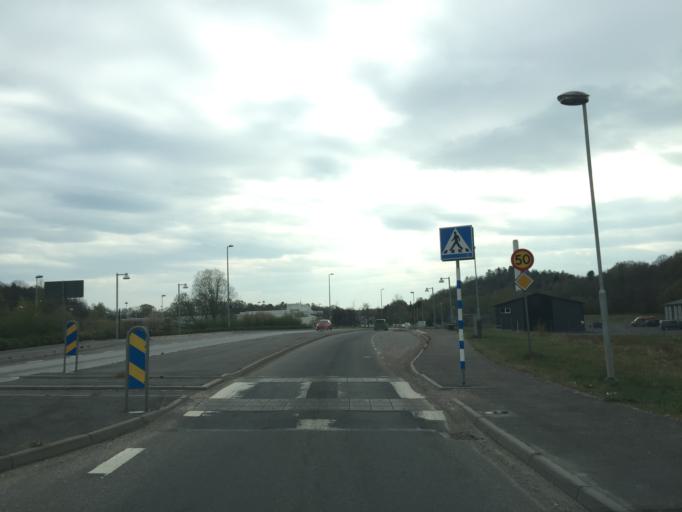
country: SE
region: Vaestra Goetaland
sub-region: Goteborg
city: Loevgaerdet
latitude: 57.8054
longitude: 12.0435
